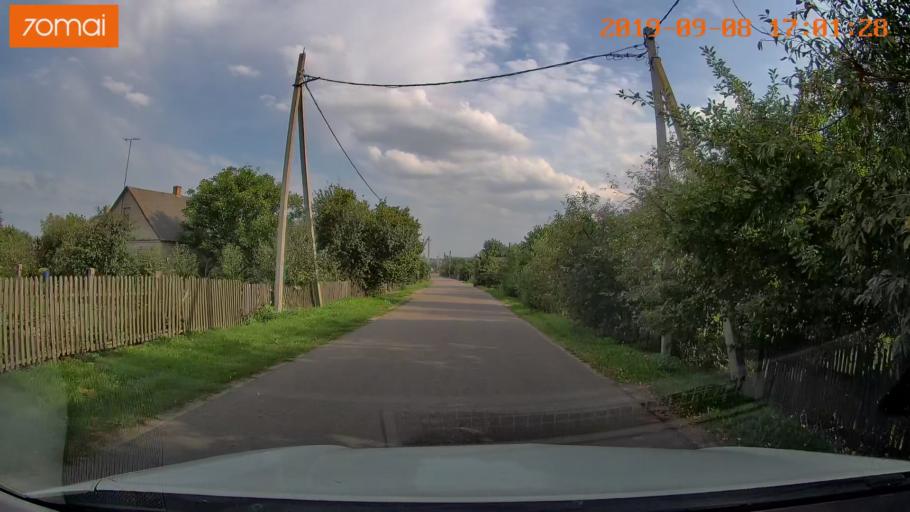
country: BY
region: Grodnenskaya
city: Hrodna
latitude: 53.7103
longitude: 23.9347
